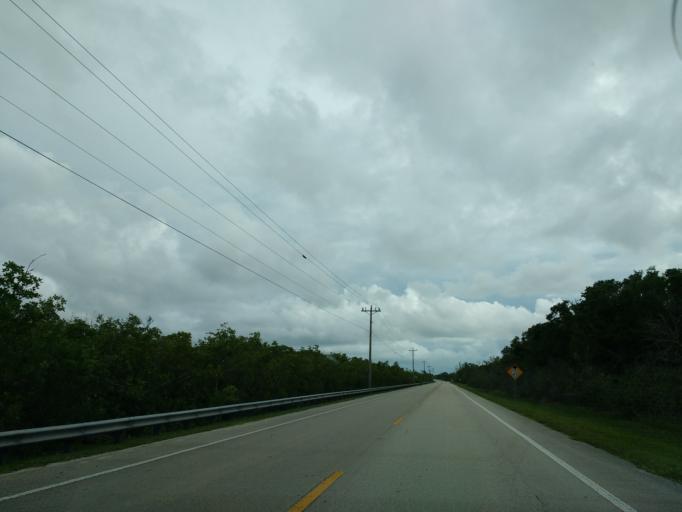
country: US
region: Florida
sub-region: Collier County
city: Marco
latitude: 25.8778
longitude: -81.3808
